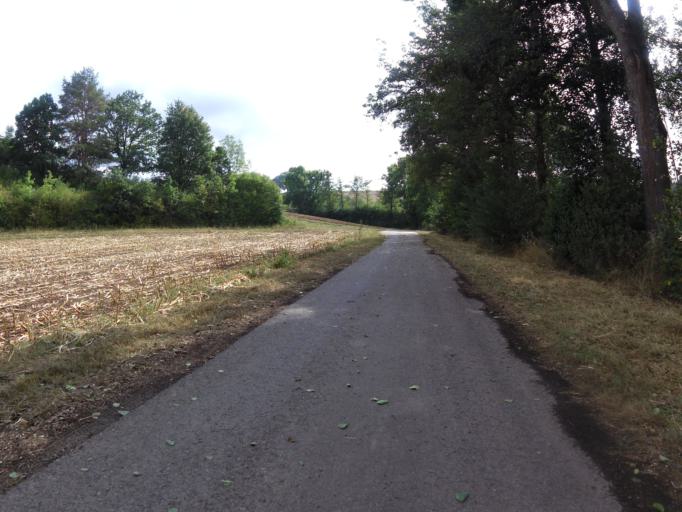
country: DE
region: Bavaria
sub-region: Regierungsbezirk Unterfranken
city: Gadheim
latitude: 49.8529
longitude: 9.9095
